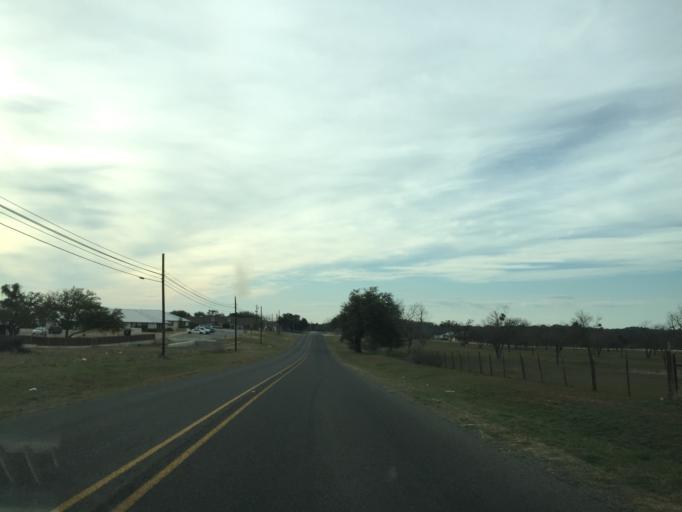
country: US
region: Texas
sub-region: Llano County
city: Llano
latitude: 30.7515
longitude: -98.6948
